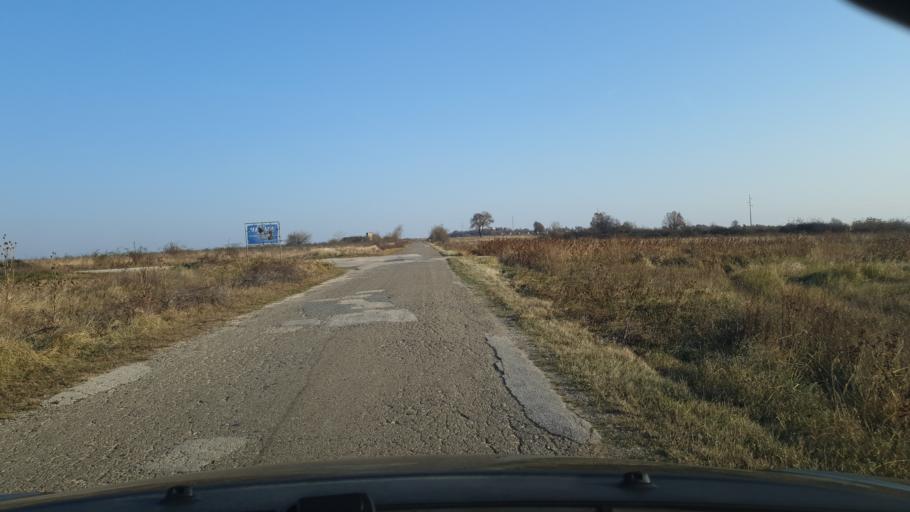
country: RS
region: Central Serbia
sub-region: Borski Okrug
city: Negotin
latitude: 44.1209
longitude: 22.3542
